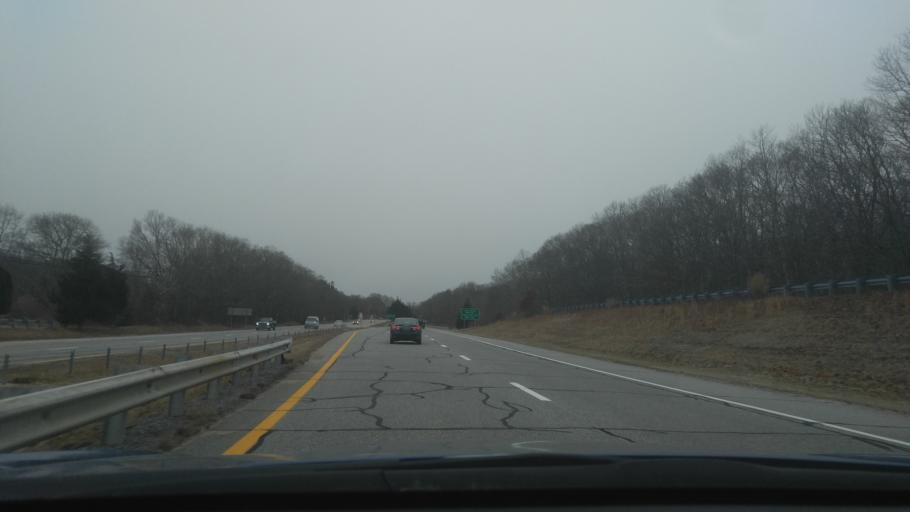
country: US
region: Rhode Island
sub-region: Washington County
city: Wakefield-Peacedale
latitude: 41.4079
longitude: -71.5324
